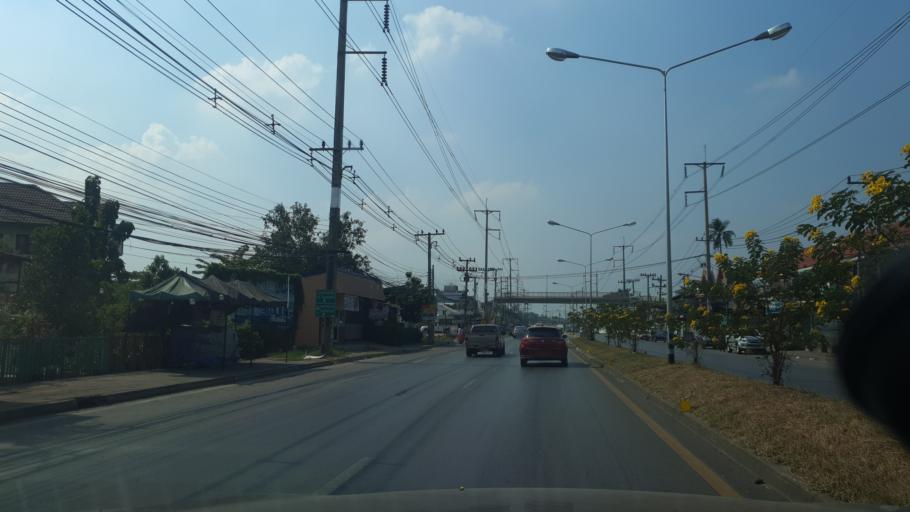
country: TH
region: Samut Sakhon
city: Krathum Baen
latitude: 13.6651
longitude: 100.2768
